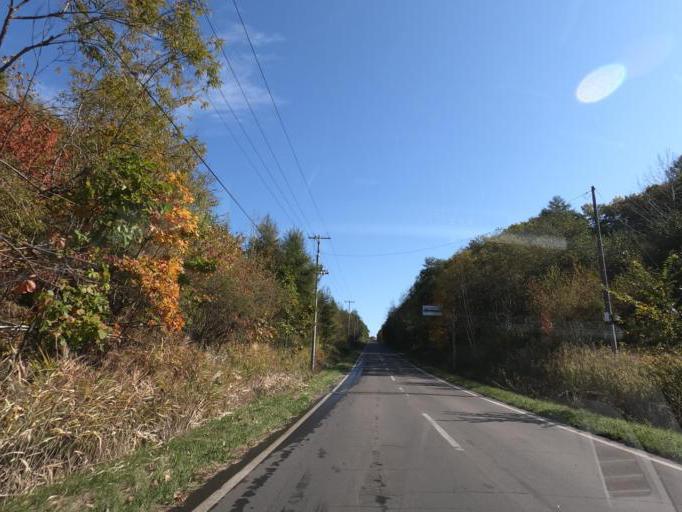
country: JP
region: Hokkaido
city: Otofuke
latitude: 42.9961
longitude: 143.2573
